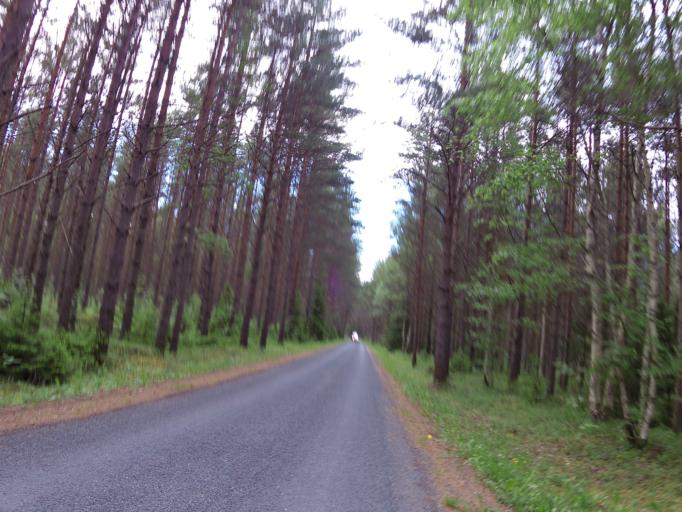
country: EE
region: Harju
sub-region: Paldiski linn
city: Paldiski
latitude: 59.2512
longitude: 23.7643
